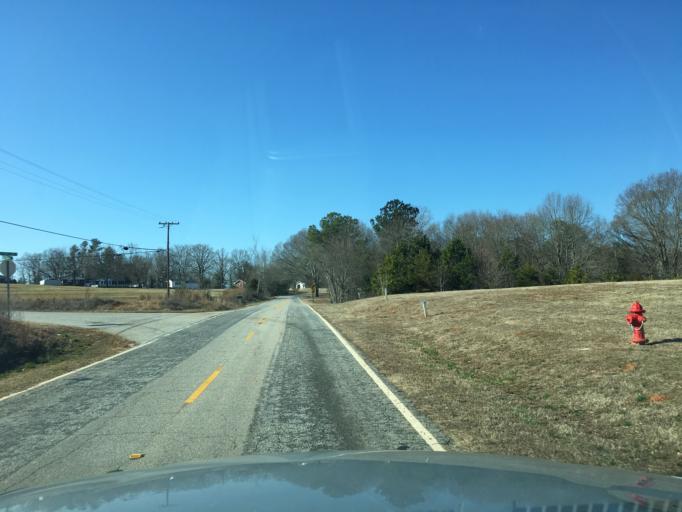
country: US
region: South Carolina
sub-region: Pickens County
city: Pickens
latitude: 34.8553
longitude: -82.7637
